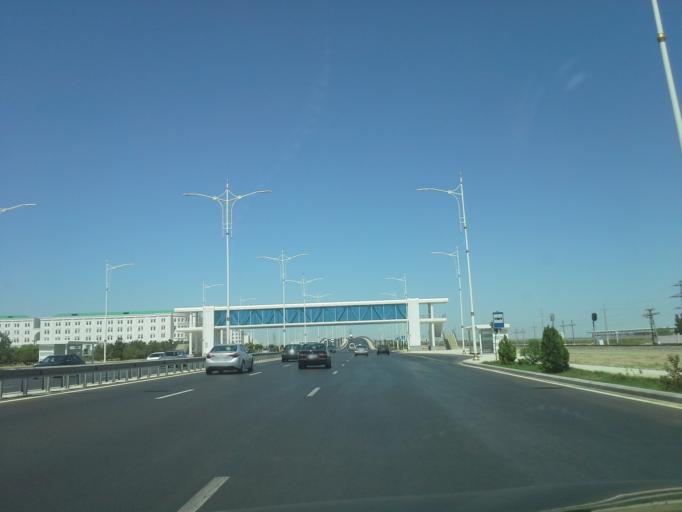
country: TM
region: Ahal
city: Ashgabat
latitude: 37.9744
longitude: 58.3471
